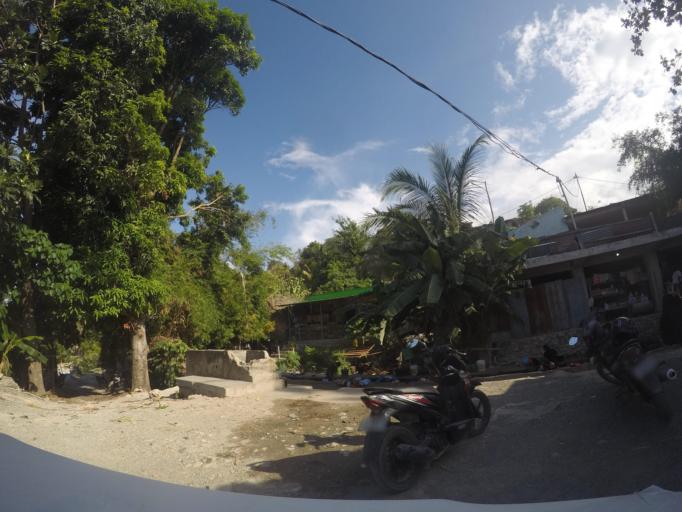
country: TL
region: Baucau
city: Baucau
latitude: -8.4619
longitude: 126.4545
